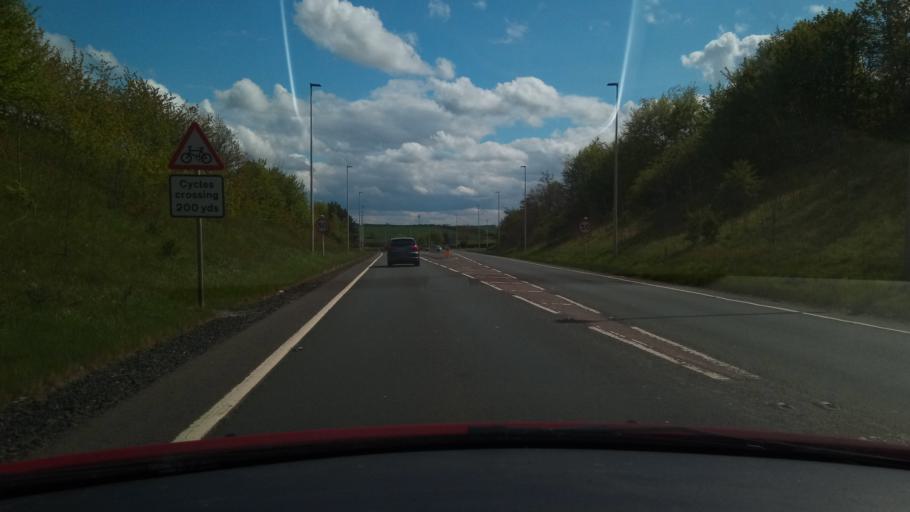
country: GB
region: Scotland
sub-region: The Scottish Borders
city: Newtown St Boswells
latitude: 55.5761
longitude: -2.6646
